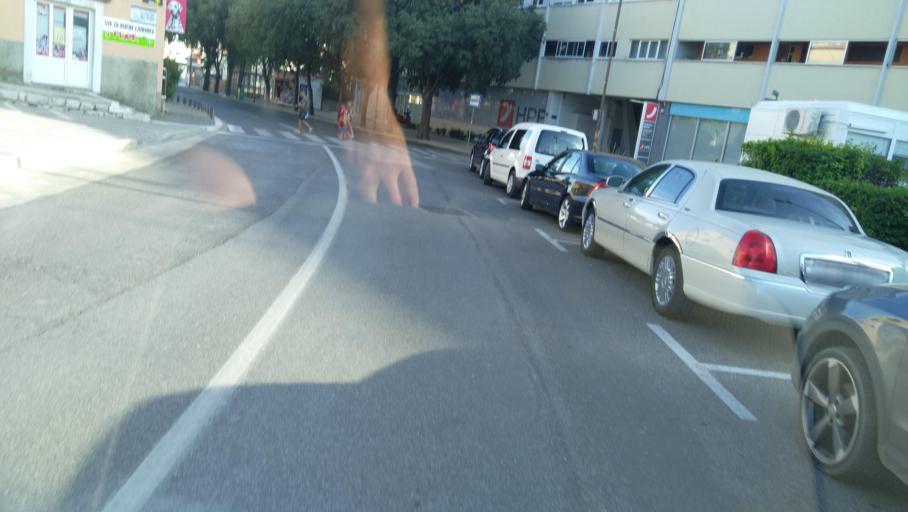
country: HR
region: Sibensko-Kniniska
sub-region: Grad Sibenik
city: Sibenik
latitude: 43.7337
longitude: 15.8951
